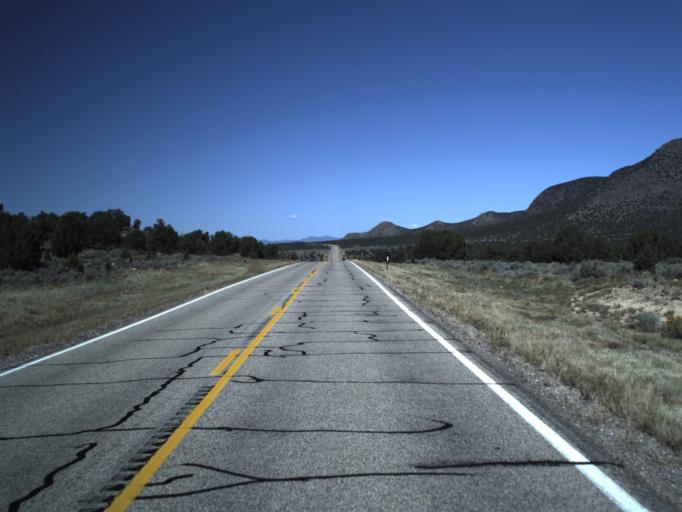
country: US
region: Utah
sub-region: Washington County
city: Enterprise
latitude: 37.6413
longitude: -113.4388
